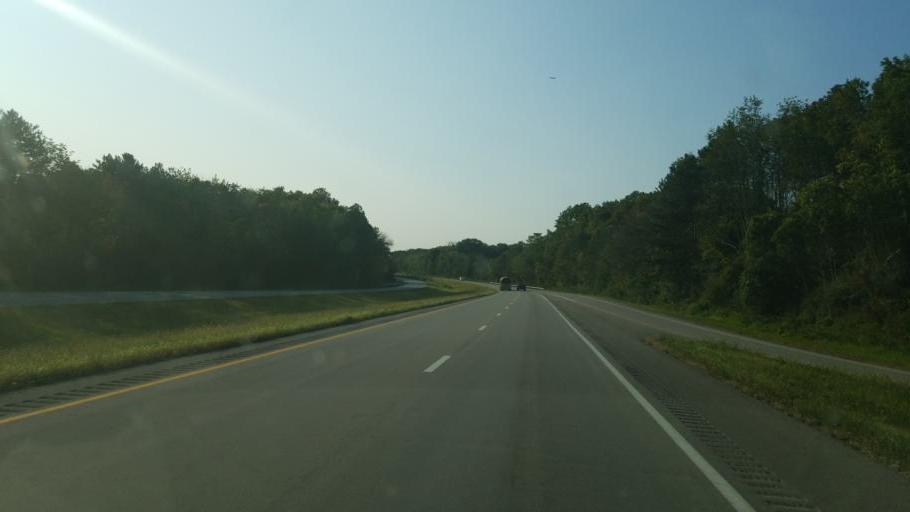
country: US
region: Ohio
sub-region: Stark County
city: Brewster
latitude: 40.7701
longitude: -81.5839
